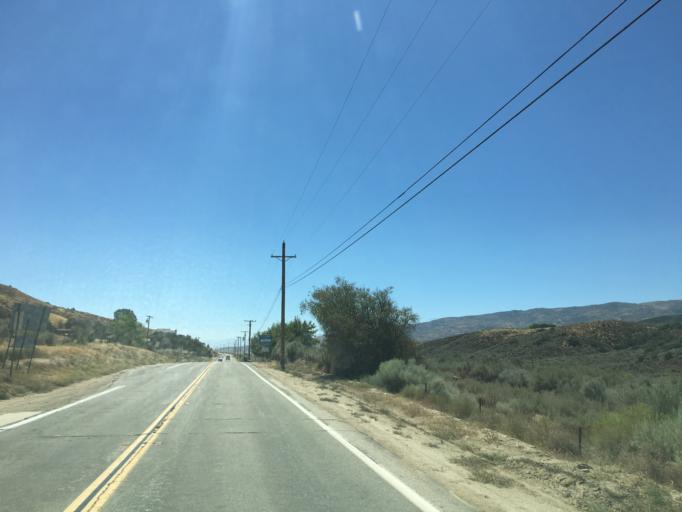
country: US
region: California
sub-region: Los Angeles County
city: Leona Valley
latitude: 34.6242
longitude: -118.3051
